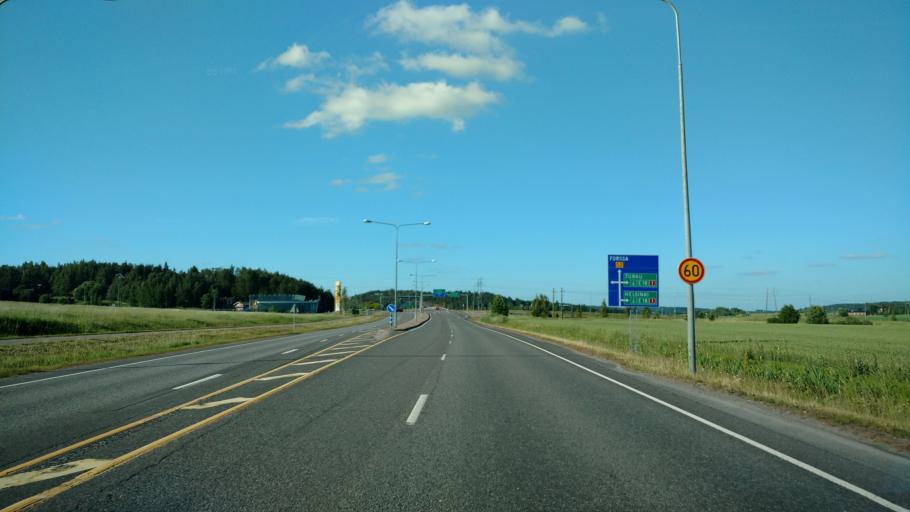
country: FI
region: Varsinais-Suomi
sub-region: Salo
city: Salo
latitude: 60.4144
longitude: 23.1621
